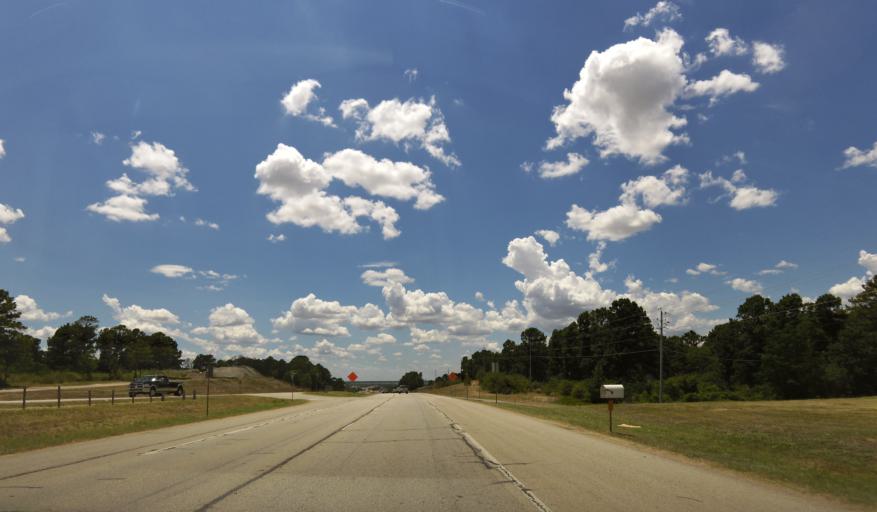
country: US
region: Texas
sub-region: Bastrop County
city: Bastrop
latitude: 30.1052
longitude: -97.2953
